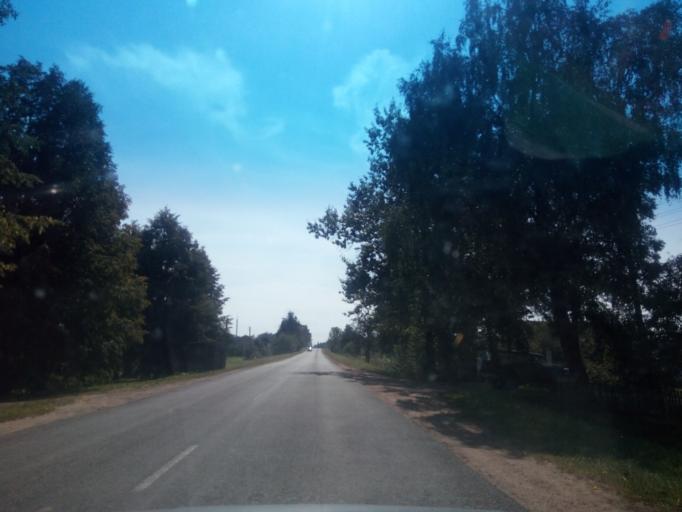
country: BY
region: Vitebsk
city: Vyerkhnyadzvinsk
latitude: 55.8268
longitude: 27.7355
